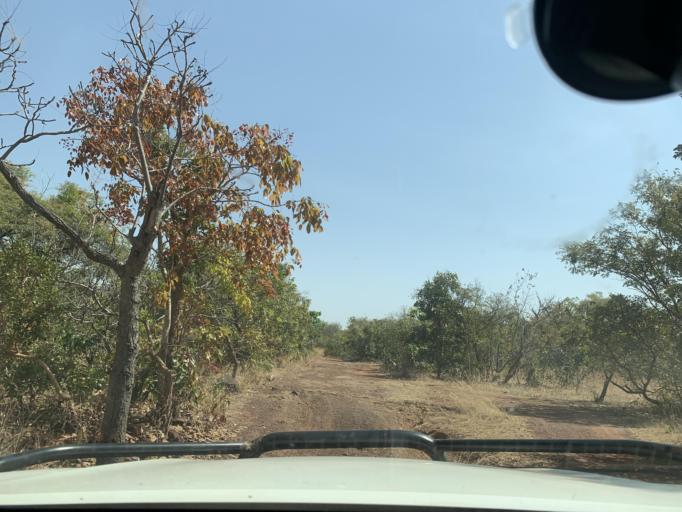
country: ML
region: Sikasso
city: Kolondieba
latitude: 10.8352
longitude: -6.7917
